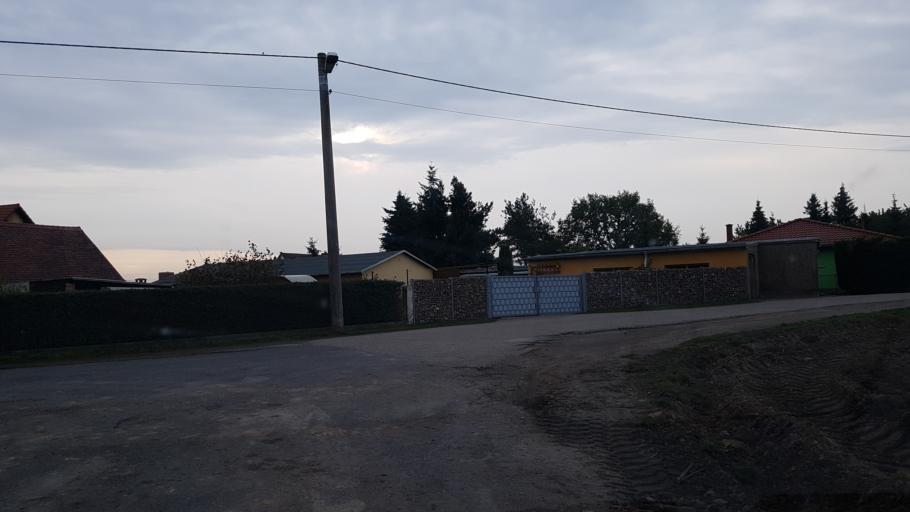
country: DE
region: Saxony
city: Dahlen
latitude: 51.3945
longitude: 12.9839
